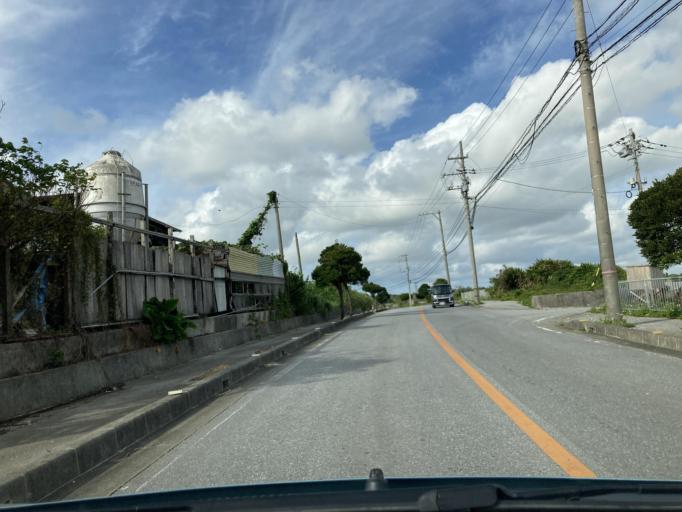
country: JP
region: Okinawa
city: Itoman
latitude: 26.1114
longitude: 127.7186
